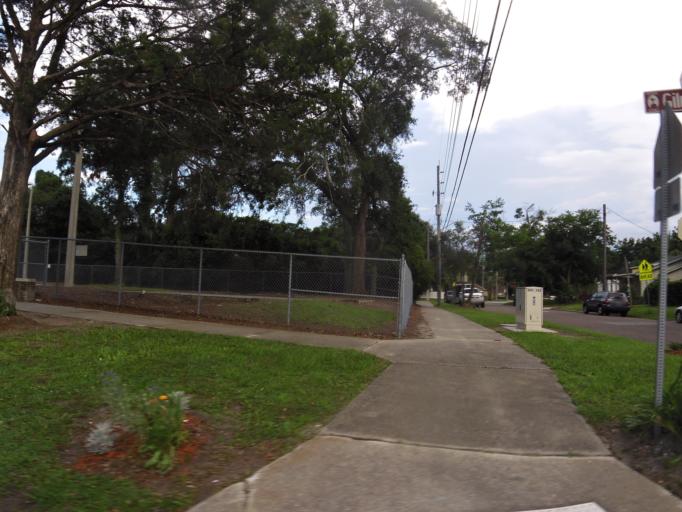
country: US
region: Florida
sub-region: Duval County
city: Jacksonville
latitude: 30.3183
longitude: -81.6924
